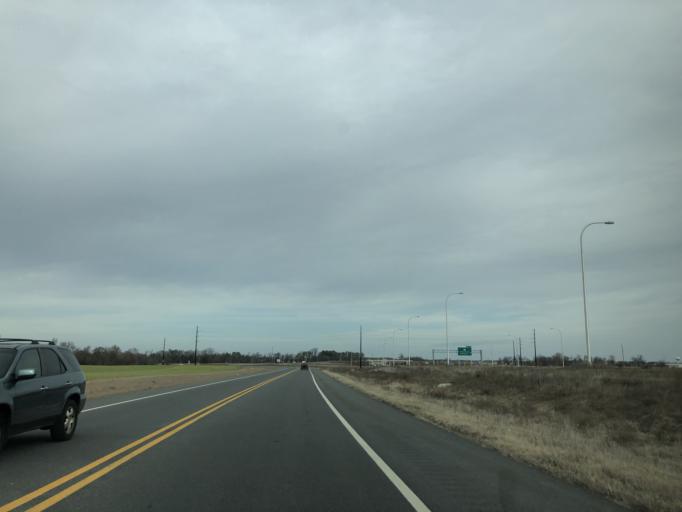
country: US
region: Delaware
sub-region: New Castle County
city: Middletown
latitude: 39.4396
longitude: -75.7575
